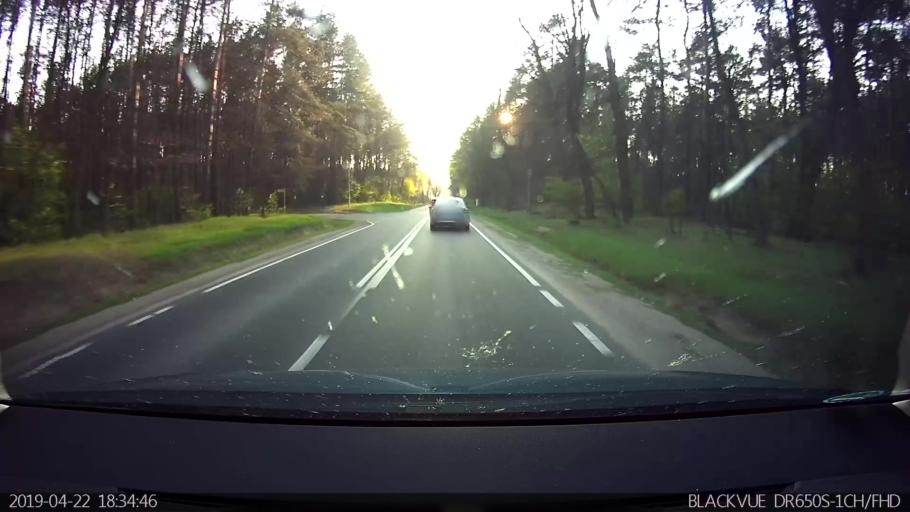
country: PL
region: Masovian Voivodeship
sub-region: Powiat wolominski
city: Klembow
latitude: 52.4456
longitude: 21.3625
